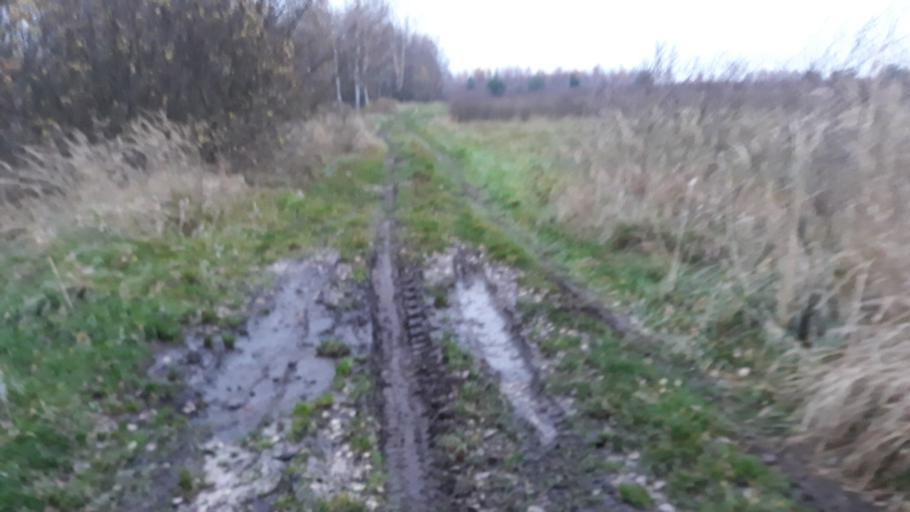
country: PL
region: Lublin Voivodeship
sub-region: Powiat janowski
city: Dzwola
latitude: 50.6678
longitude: 22.5802
